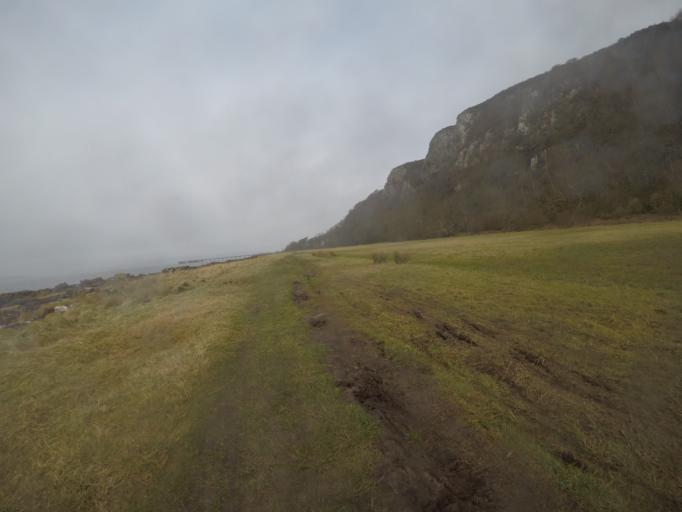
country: GB
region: Scotland
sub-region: North Ayrshire
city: Millport
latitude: 55.7096
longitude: -4.9040
